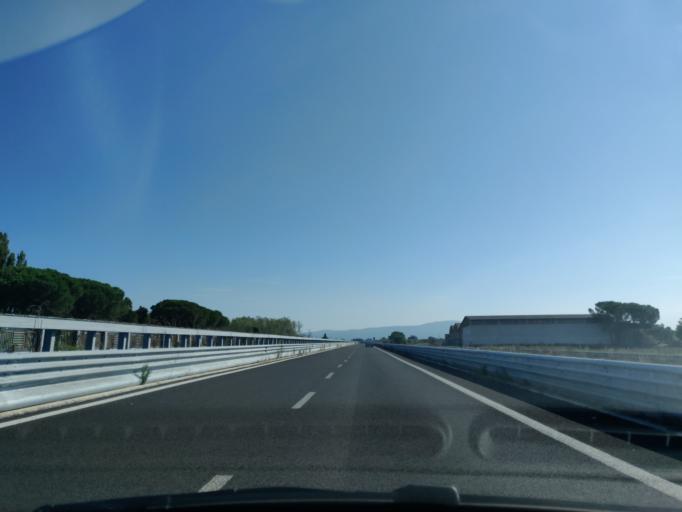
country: IT
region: Latium
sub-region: Provincia di Viterbo
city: Blera
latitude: 42.3011
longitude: 11.9752
